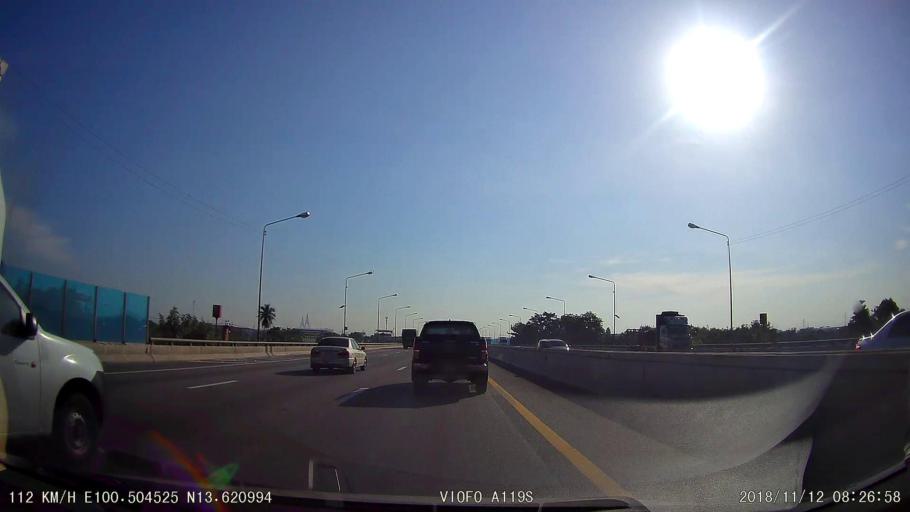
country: TH
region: Bangkok
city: Thung Khru
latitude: 13.6210
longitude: 100.5049
